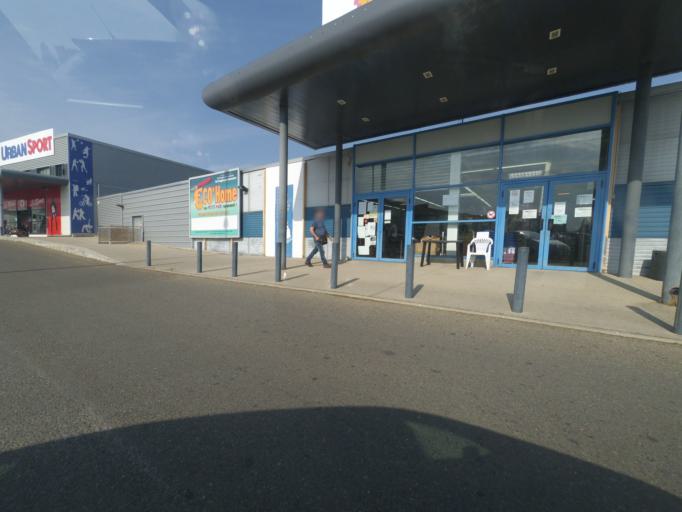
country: FR
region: Languedoc-Roussillon
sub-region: Departement du Gard
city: Sommieres
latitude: 43.7799
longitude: 4.0788
